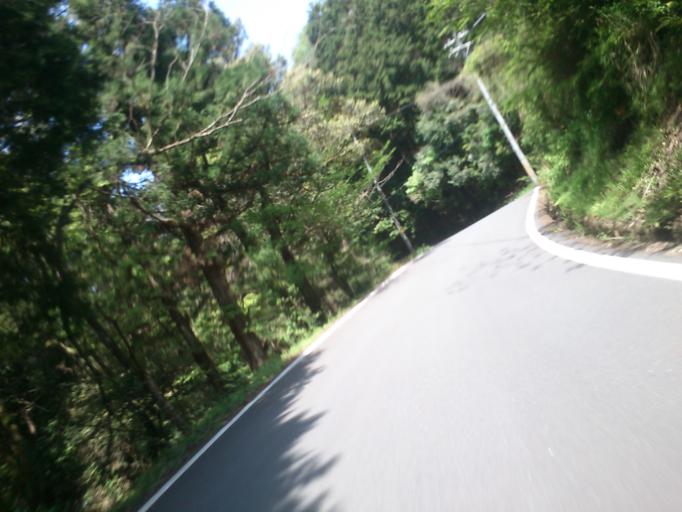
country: JP
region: Kyoto
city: Miyazu
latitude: 35.6125
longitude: 135.2154
